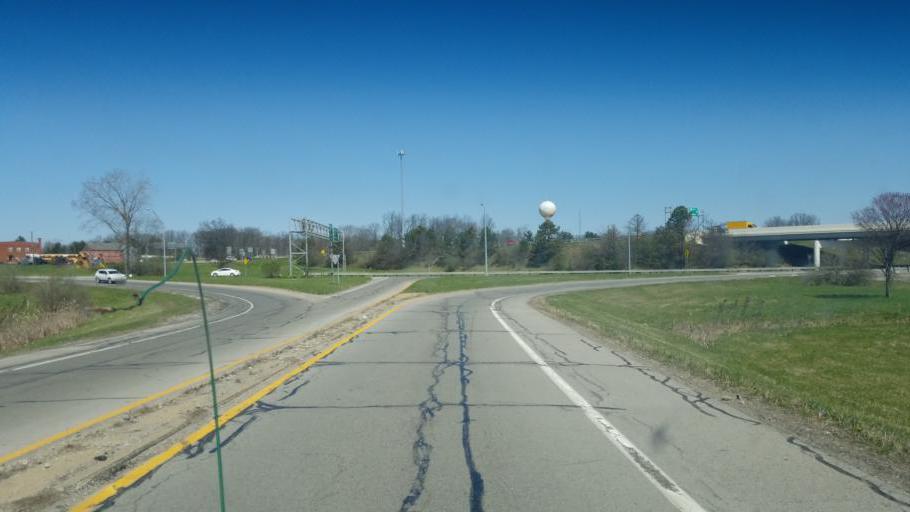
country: US
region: Ohio
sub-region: Richland County
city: Lincoln Heights
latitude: 40.7779
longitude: -82.4707
